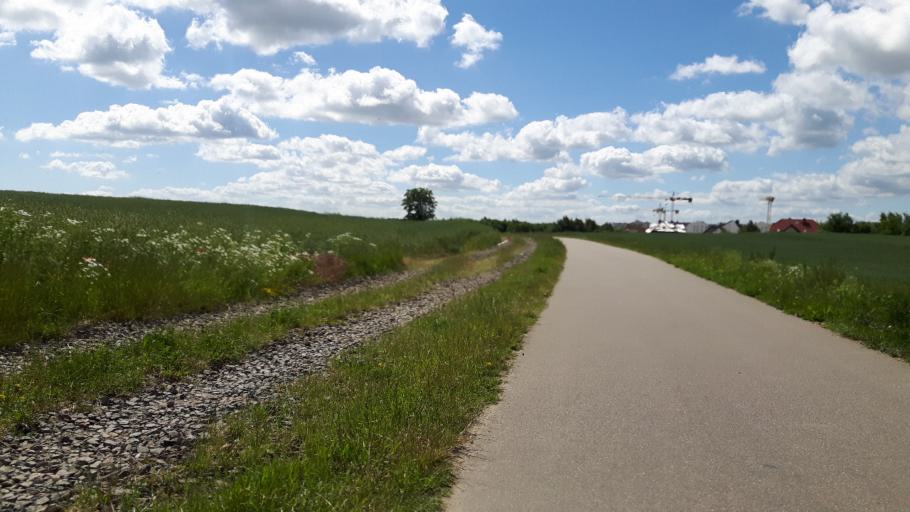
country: PL
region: Pomeranian Voivodeship
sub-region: Powiat pucki
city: Kosakowo
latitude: 54.5756
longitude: 18.4966
